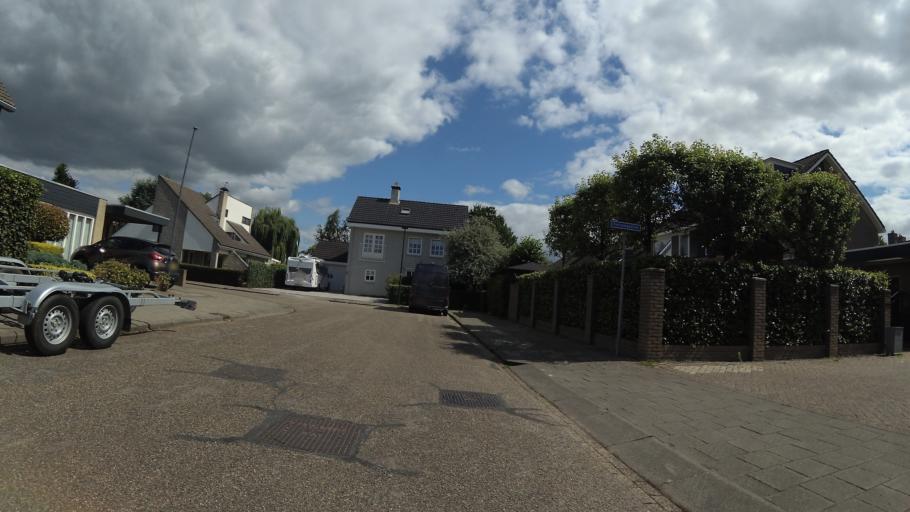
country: NL
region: North Brabant
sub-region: Gemeente Dongen
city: Dongen
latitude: 51.6357
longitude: 4.9484
